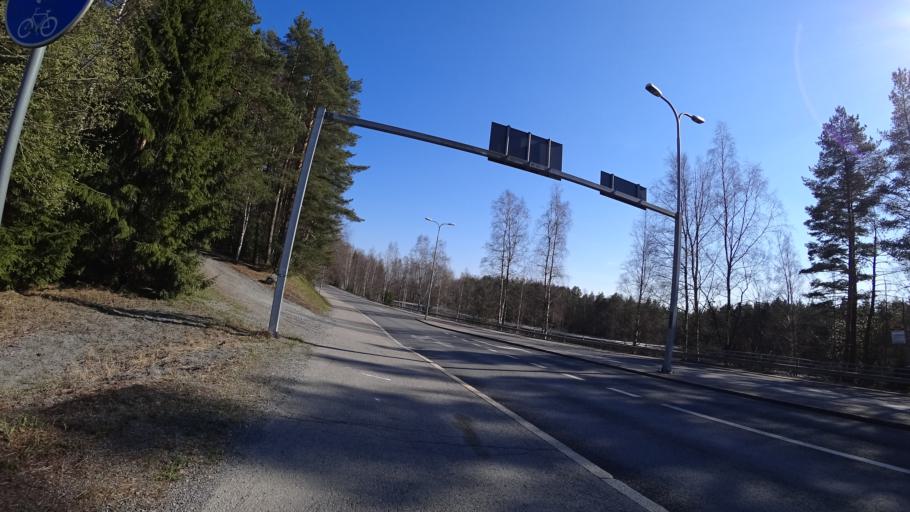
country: FI
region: Pirkanmaa
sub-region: Tampere
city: Pirkkala
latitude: 61.5190
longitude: 23.6442
